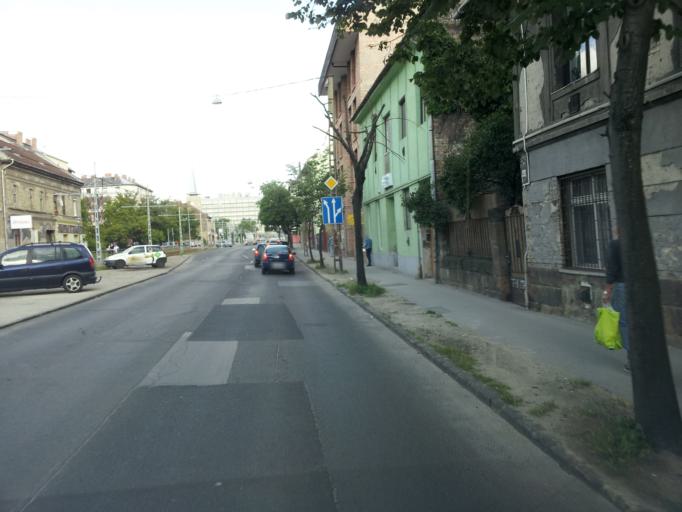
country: HU
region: Budapest
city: Budapest XIV. keruelet
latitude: 47.5206
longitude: 19.1081
